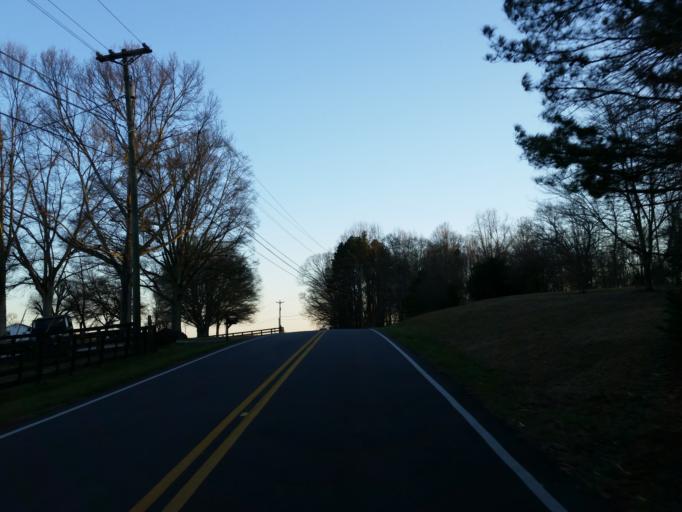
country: US
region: Georgia
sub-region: Cherokee County
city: Holly Springs
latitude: 34.1494
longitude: -84.4354
